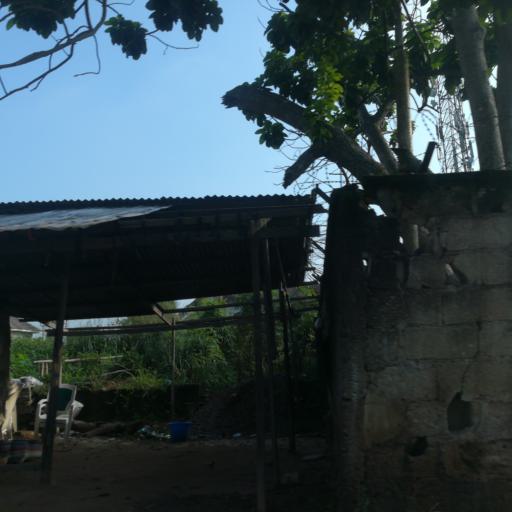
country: NG
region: Rivers
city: Port Harcourt
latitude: 4.8581
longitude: 6.9652
